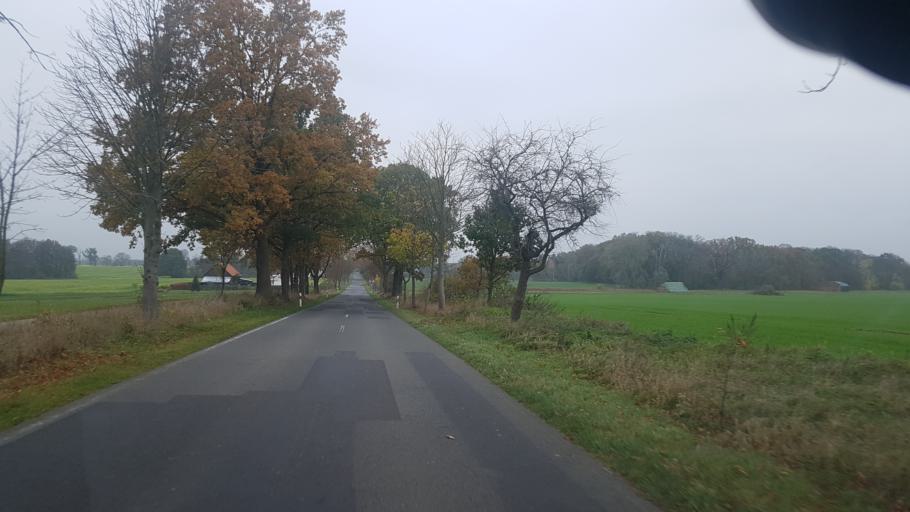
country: DE
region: Brandenburg
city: Schonermark
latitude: 52.9122
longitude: 13.1357
